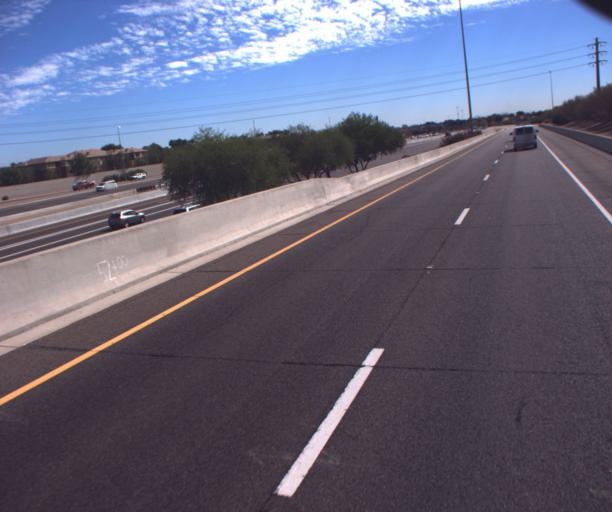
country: US
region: Arizona
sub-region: Maricopa County
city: Chandler
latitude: 33.2900
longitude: -111.8863
